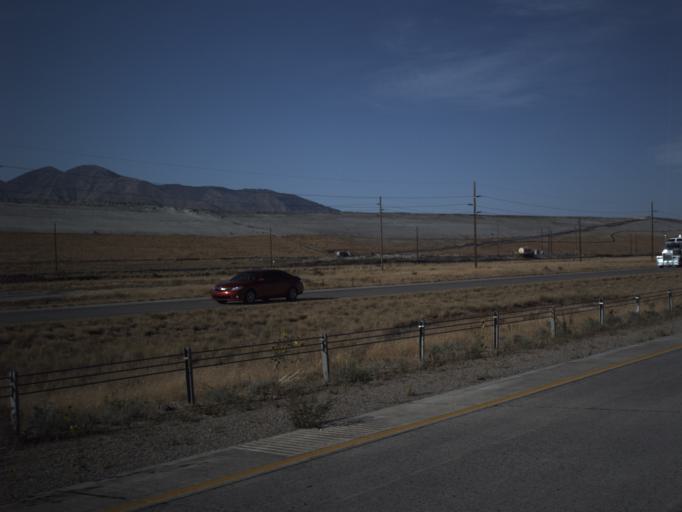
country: US
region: Utah
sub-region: Salt Lake County
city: Magna
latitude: 40.7710
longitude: -112.1156
